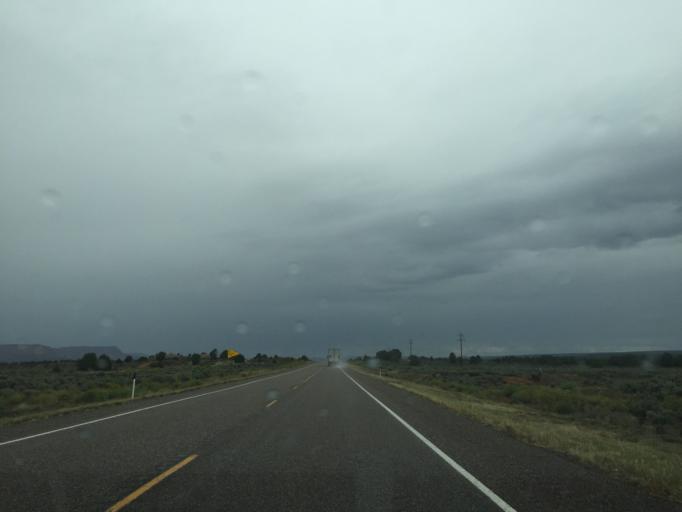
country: US
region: Utah
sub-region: Kane County
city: Kanab
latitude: 37.1026
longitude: -112.1294
